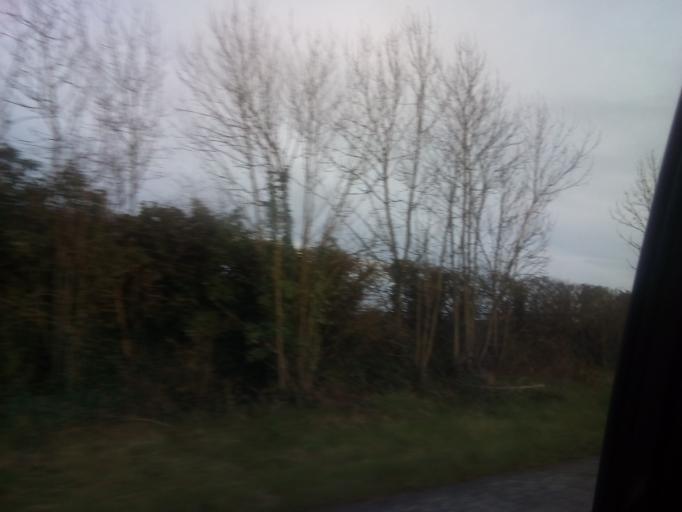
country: IE
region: Leinster
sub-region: Laois
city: Abbeyleix
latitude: 52.8554
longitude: -7.3862
